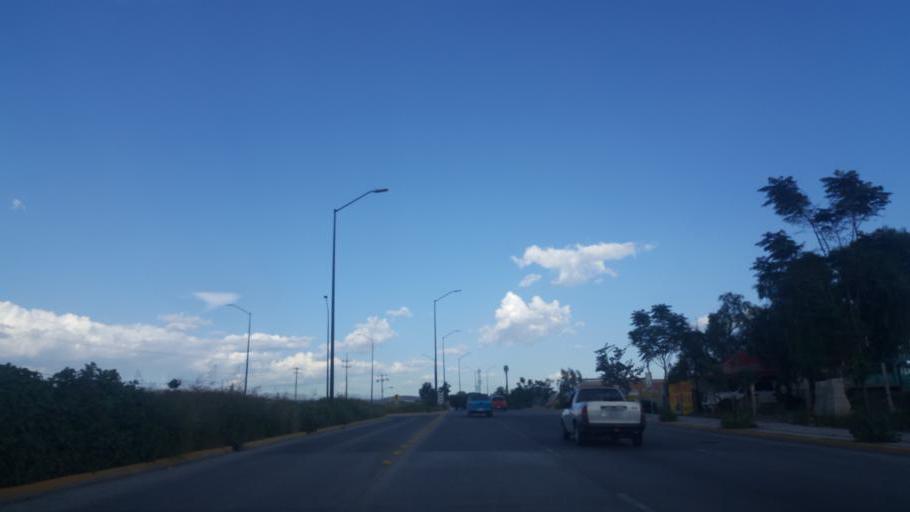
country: MX
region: Guanajuato
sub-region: Leon
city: San Jose de Duran (Los Troncoso)
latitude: 21.0961
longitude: -101.7009
